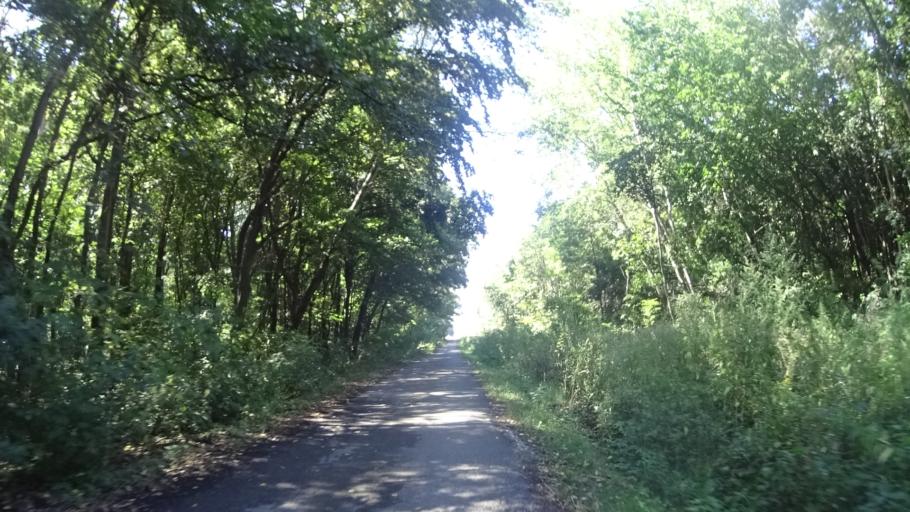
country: AT
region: Lower Austria
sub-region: Politischer Bezirk Ganserndorf
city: Angern an der March
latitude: 48.3703
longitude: 16.8571
